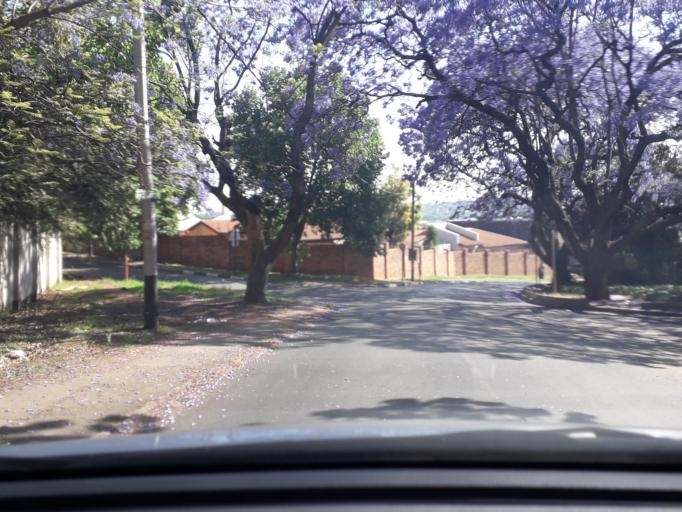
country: ZA
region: Gauteng
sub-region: City of Johannesburg Metropolitan Municipality
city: Johannesburg
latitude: -26.1441
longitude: 27.9785
